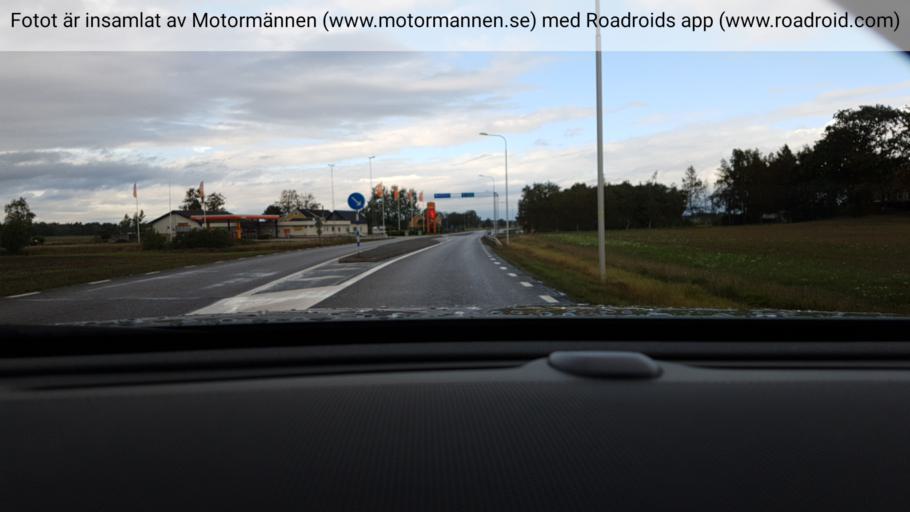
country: SE
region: Vaestra Goetaland
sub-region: Vanersborgs Kommun
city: Vanersborg
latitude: 58.4740
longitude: 12.2680
